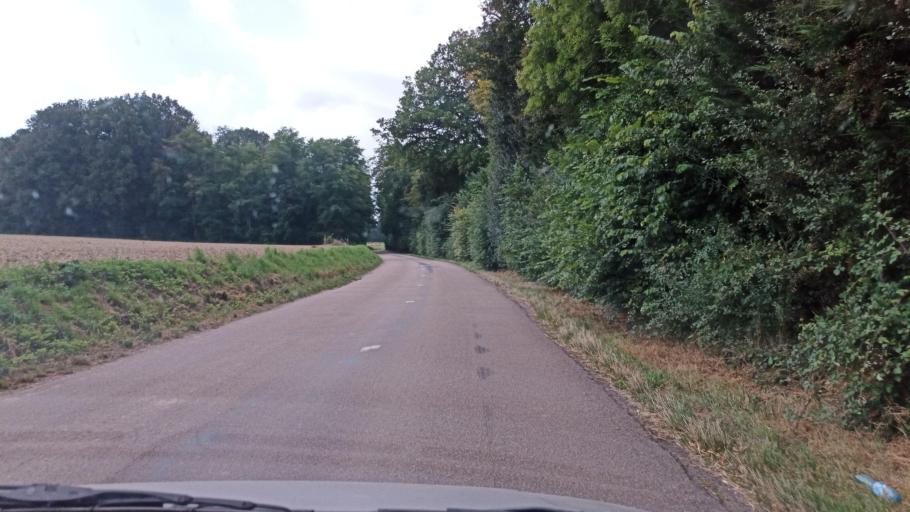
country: FR
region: Bourgogne
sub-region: Departement de l'Yonne
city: Egriselles-le-Bocage
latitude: 48.0195
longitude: 3.1699
